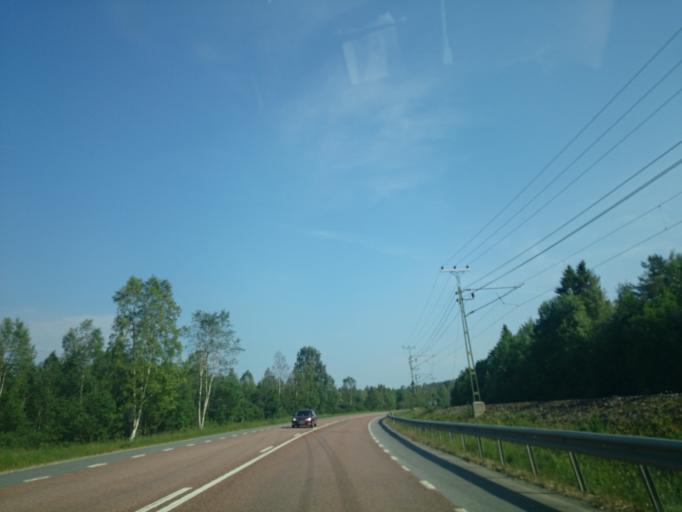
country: SE
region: Jaemtland
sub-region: Braecke Kommun
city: Braecke
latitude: 62.9148
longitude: 15.2588
